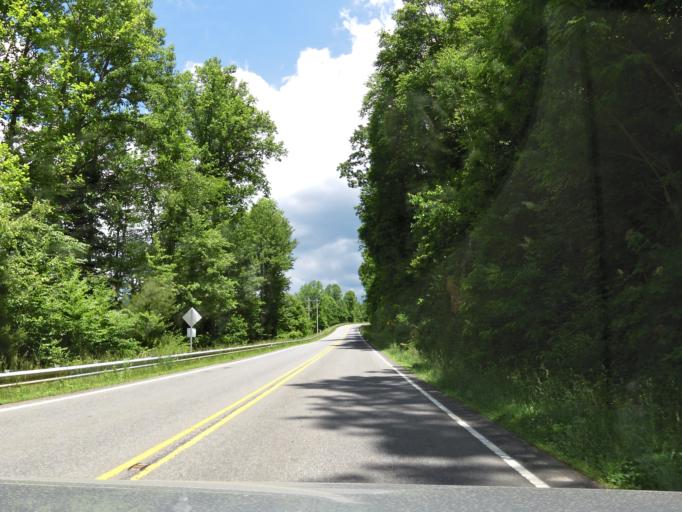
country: US
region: North Carolina
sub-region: Graham County
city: Robbinsville
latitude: 35.2726
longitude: -83.6945
